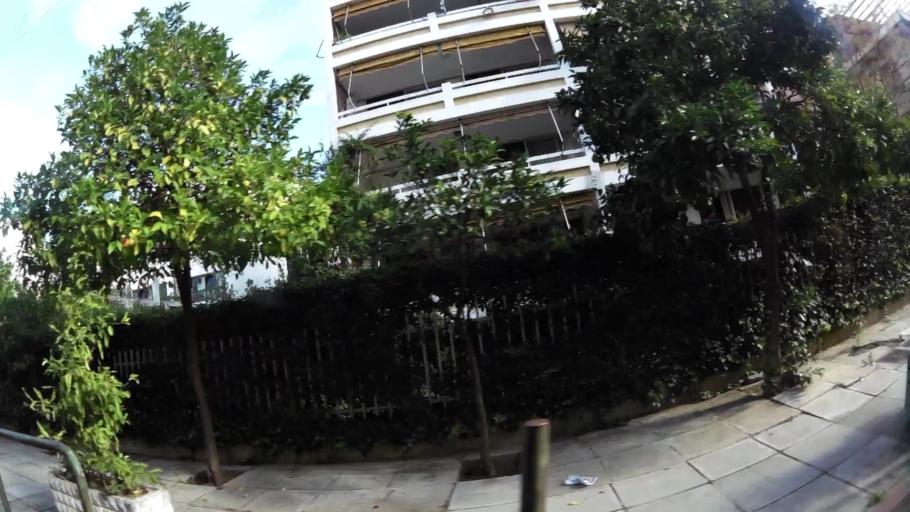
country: GR
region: Attica
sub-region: Nomarchia Athinas
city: Melissia
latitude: 38.0518
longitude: 23.8175
